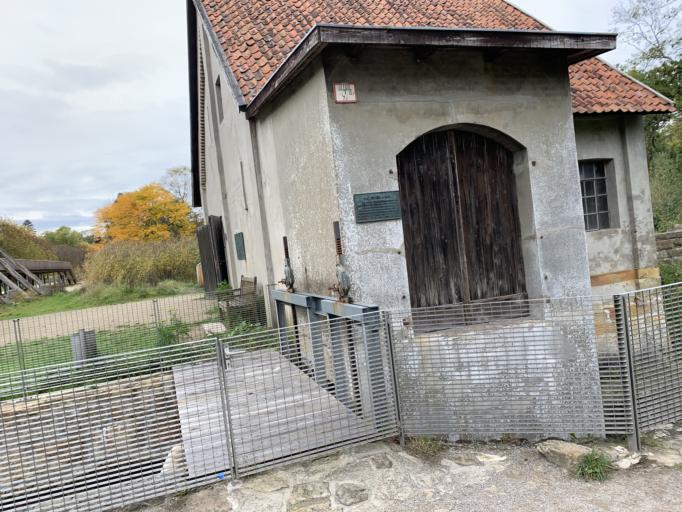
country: DE
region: North Rhine-Westphalia
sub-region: Regierungsbezirk Munster
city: Rheine
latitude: 52.2982
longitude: 7.4240
